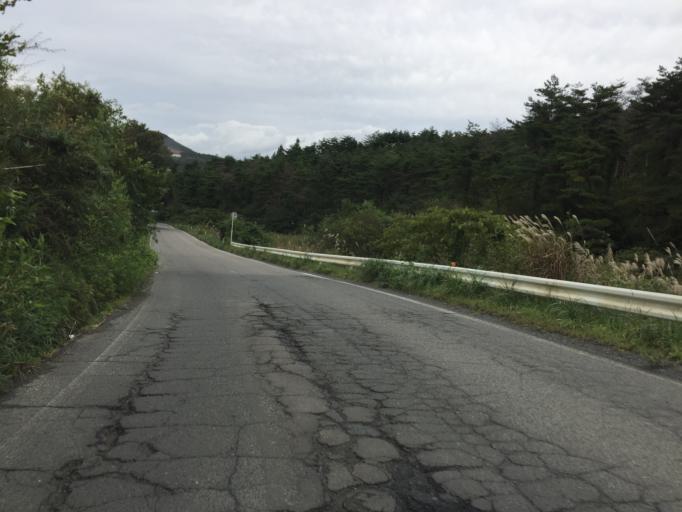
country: JP
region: Miyagi
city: Marumori
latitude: 37.8929
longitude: 140.7163
